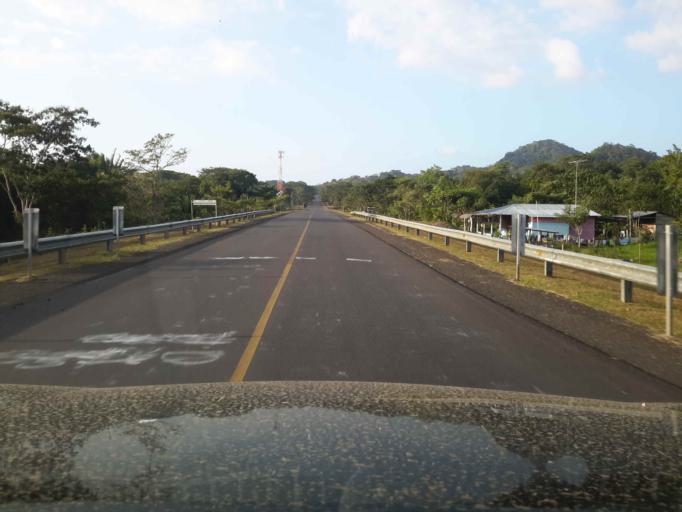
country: NI
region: Rio San Juan
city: San Miguelito
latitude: 11.3524
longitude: -84.7600
